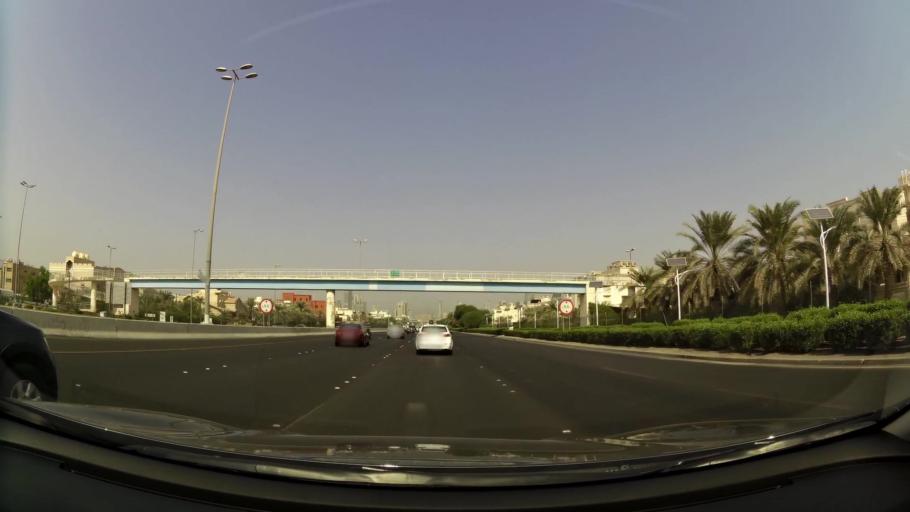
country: KW
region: Al Asimah
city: Ad Dasmah
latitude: 29.3434
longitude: 47.9988
